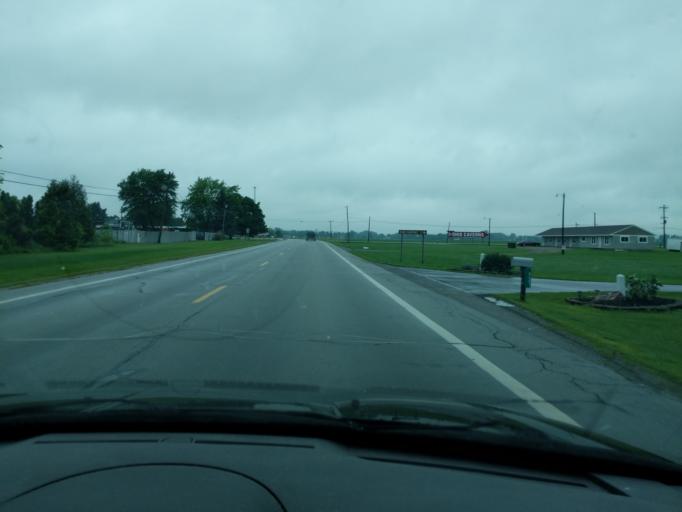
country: US
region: Ohio
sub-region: Logan County
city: West Liberty
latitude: 40.2344
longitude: -83.7518
